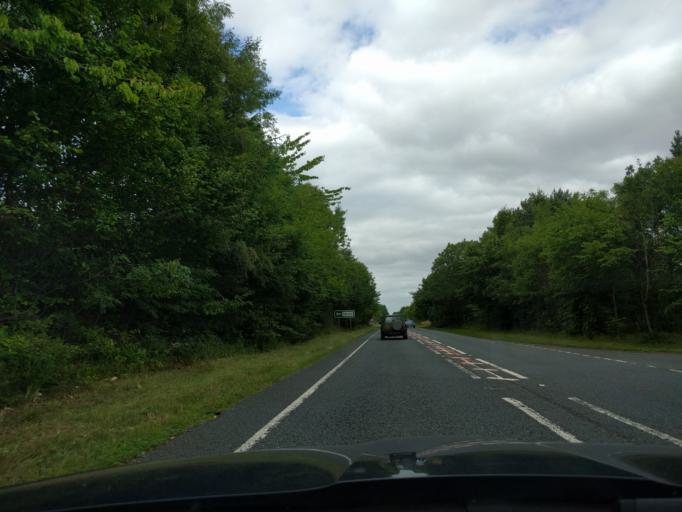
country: GB
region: England
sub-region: Northumberland
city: Belford
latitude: 55.5543
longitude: -1.7886
